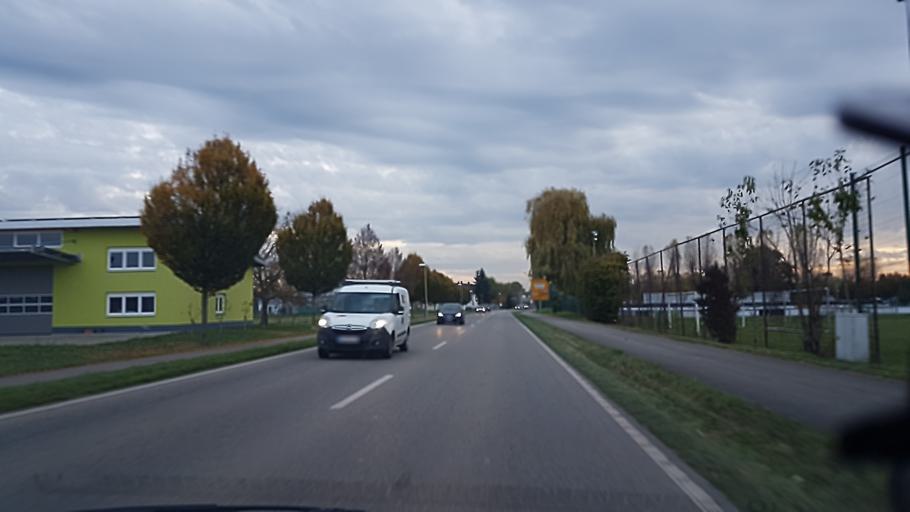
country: DE
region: Baden-Wuerttemberg
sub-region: Freiburg Region
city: Herbolzheim
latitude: 48.2280
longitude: 7.7624
